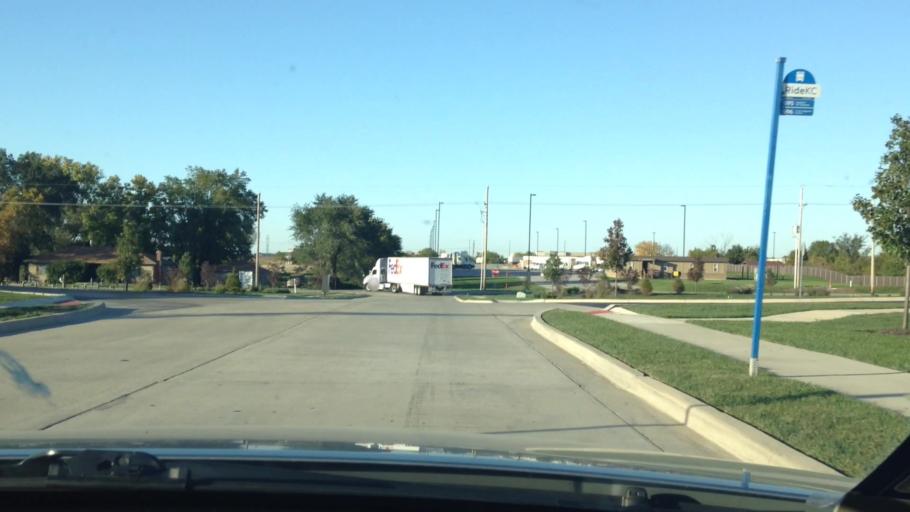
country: US
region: Kansas
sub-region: Johnson County
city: Gardner
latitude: 38.7810
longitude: -94.9423
